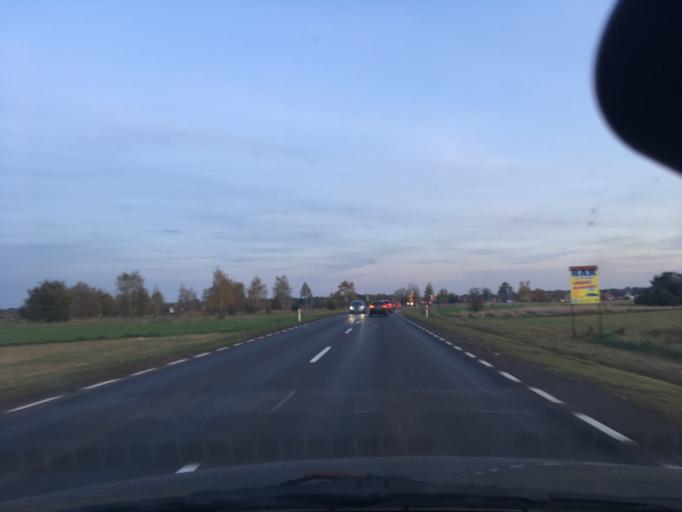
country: PL
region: Masovian Voivodeship
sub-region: Powiat plocki
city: Wyszogrod
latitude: 52.3597
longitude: 20.2043
